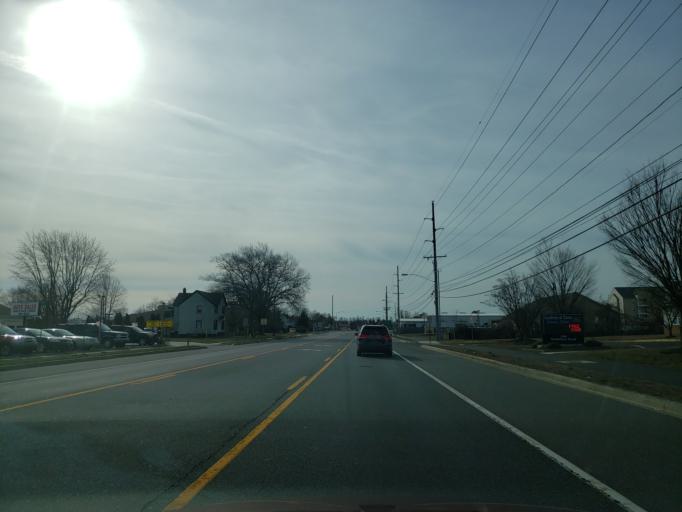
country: US
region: Delaware
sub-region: Kent County
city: Dover
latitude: 39.1622
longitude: -75.5440
